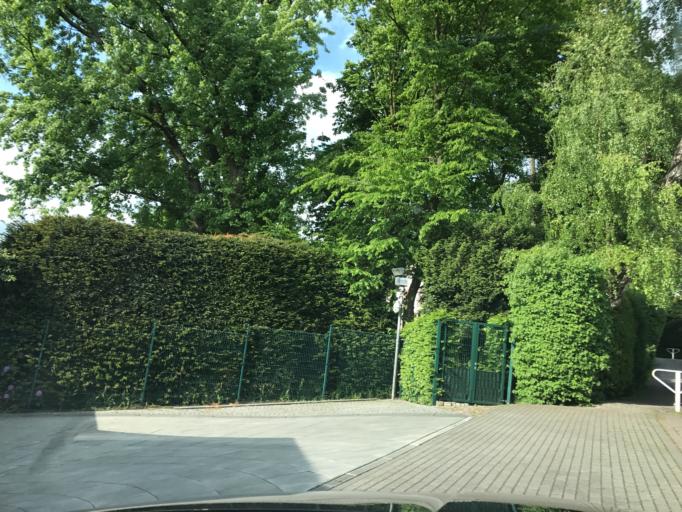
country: DE
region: North Rhine-Westphalia
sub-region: Regierungsbezirk Dusseldorf
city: Essen
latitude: 51.4061
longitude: 6.9754
